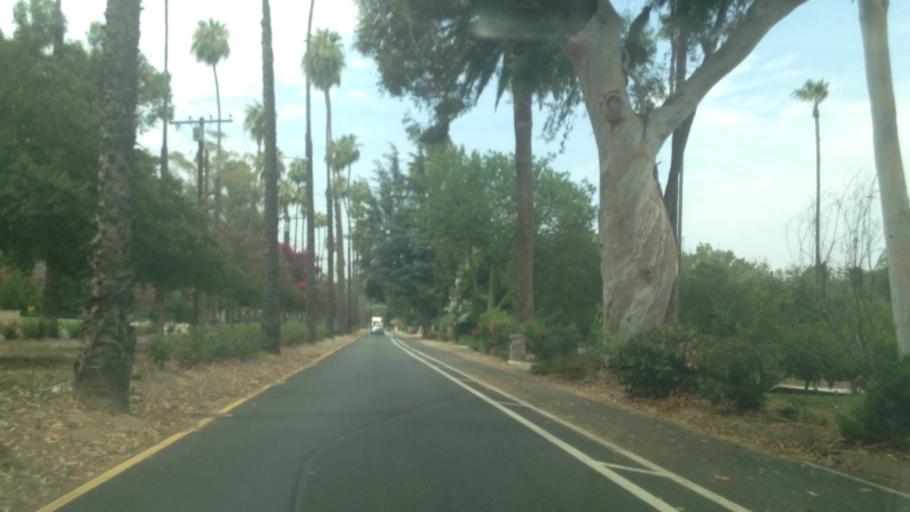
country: US
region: California
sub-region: Riverside County
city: Riverside
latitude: 33.9000
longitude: -117.4423
